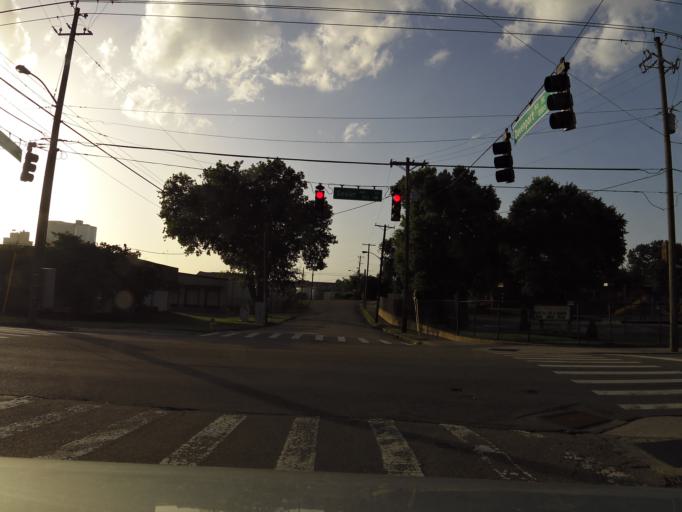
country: US
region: Tennessee
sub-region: Knox County
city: Knoxville
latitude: 35.9578
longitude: -83.9079
